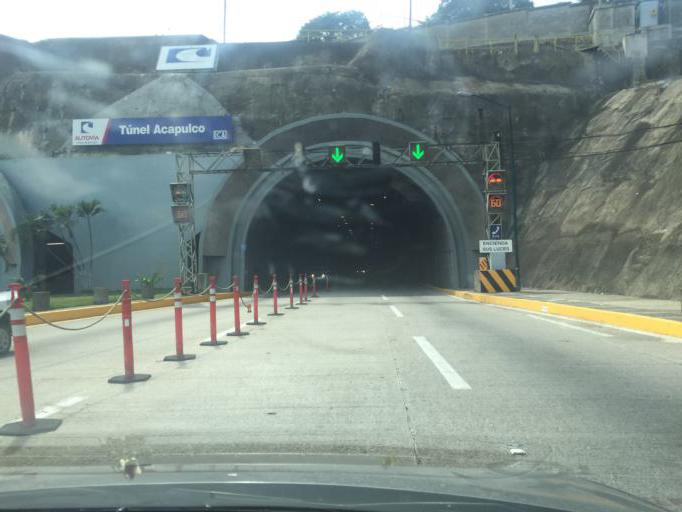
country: MX
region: Guerrero
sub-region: Acapulco de Juarez
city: Colonia Alborada
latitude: 16.8854
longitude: -99.8405
